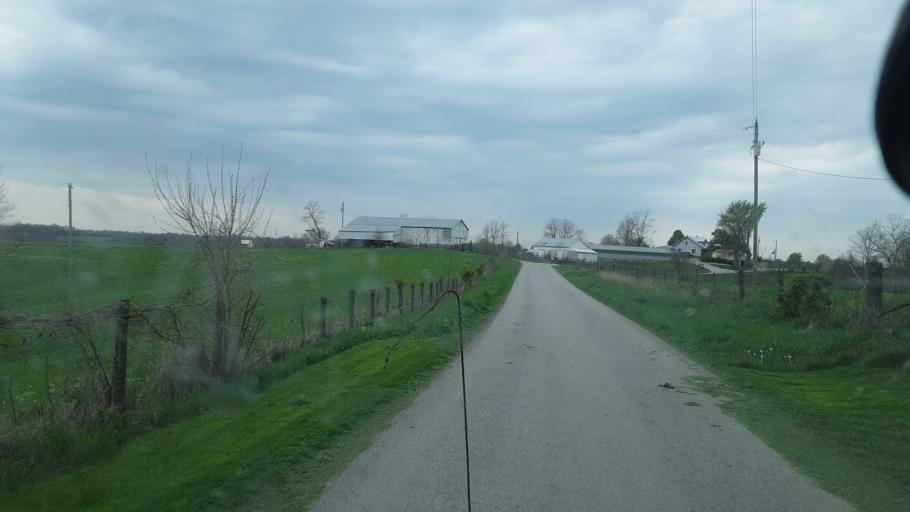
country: US
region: Kentucky
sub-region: Owen County
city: Owenton
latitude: 38.6096
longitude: -84.7769
